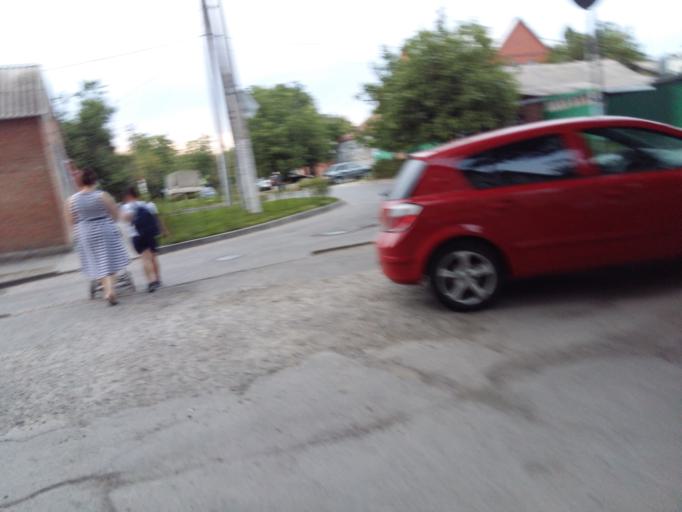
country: RU
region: Rostov
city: Imeni Chkalova
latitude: 47.2765
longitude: 39.7419
